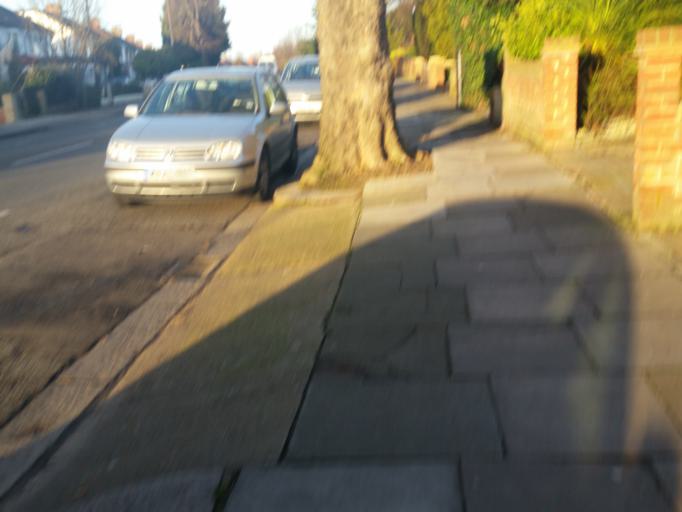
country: GB
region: England
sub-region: Greater London
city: Enfield
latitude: 51.6379
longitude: -0.0803
